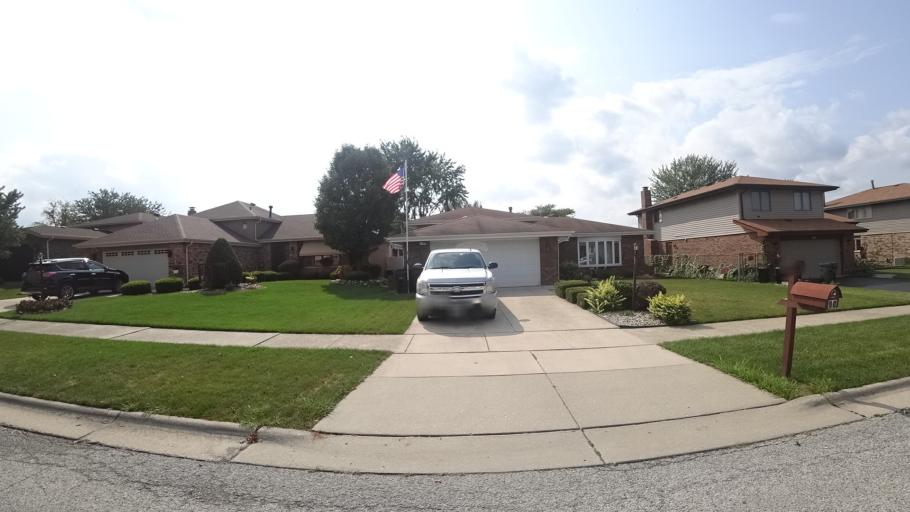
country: US
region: Illinois
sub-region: Cook County
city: Oak Forest
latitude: 41.6086
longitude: -87.7703
